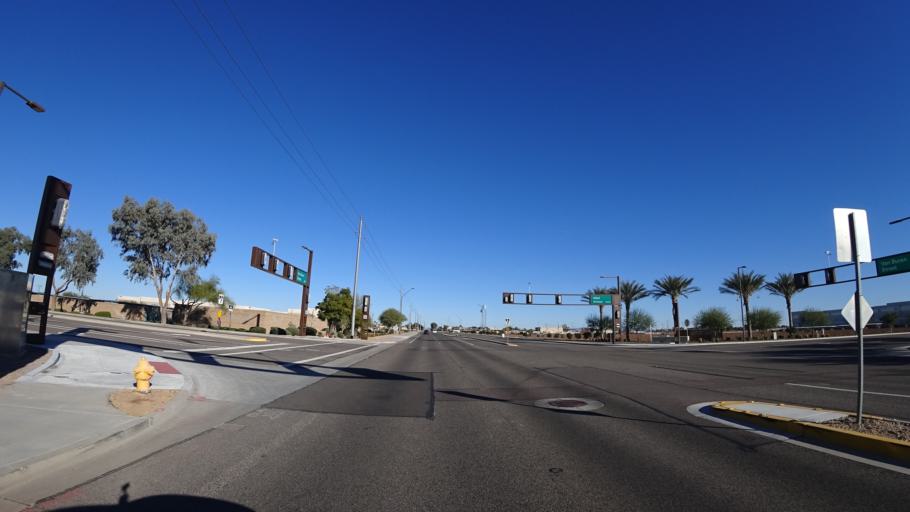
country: US
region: Arizona
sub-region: Maricopa County
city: Goodyear
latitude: 33.4499
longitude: -112.3669
